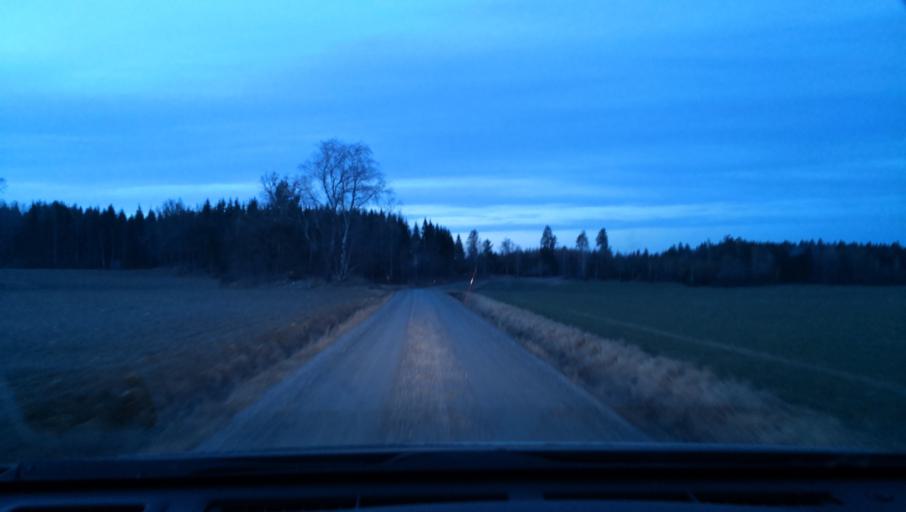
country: SE
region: Uppsala
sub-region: Enkopings Kommun
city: Dalby
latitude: 59.5589
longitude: 17.3712
